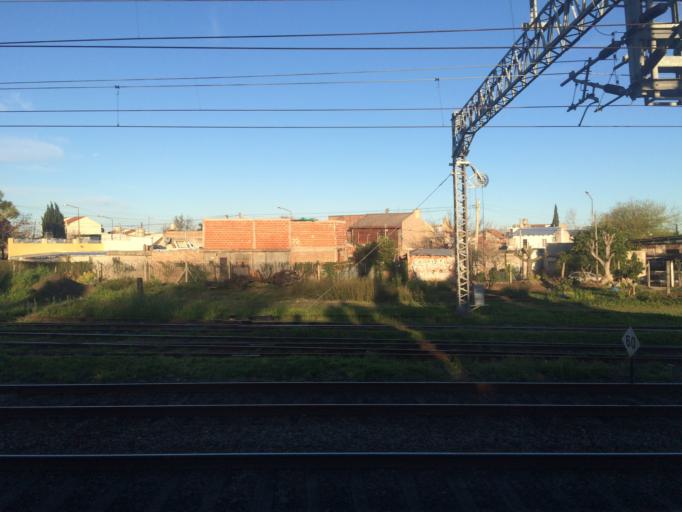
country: AR
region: Buenos Aires
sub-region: Partido de Lanus
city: Lanus
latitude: -34.6926
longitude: -58.3851
